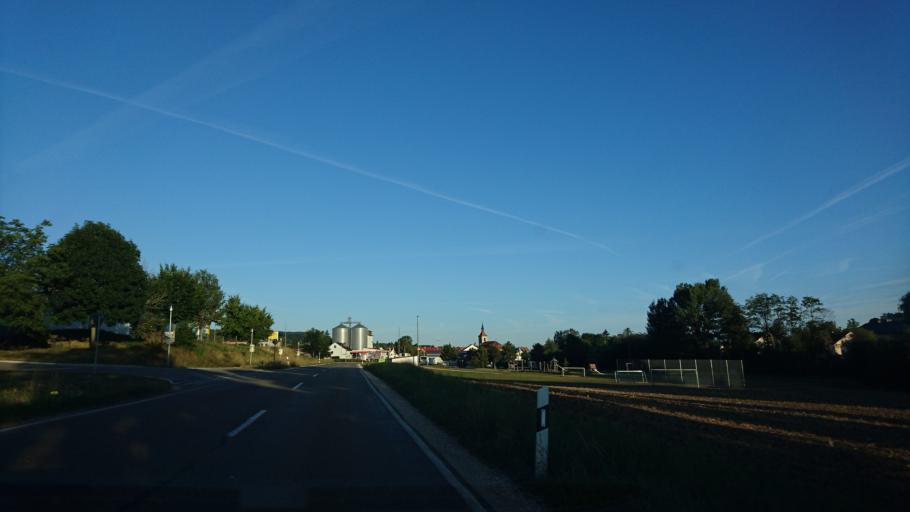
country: DE
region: Bavaria
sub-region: Regierungsbezirk Mittelfranken
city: Thalmassing
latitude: 49.0866
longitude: 11.2295
